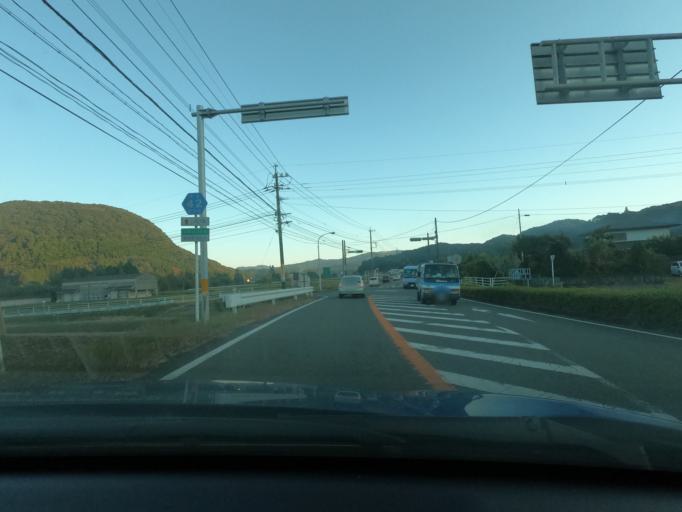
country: JP
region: Kagoshima
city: Satsumasendai
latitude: 31.8037
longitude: 130.3977
